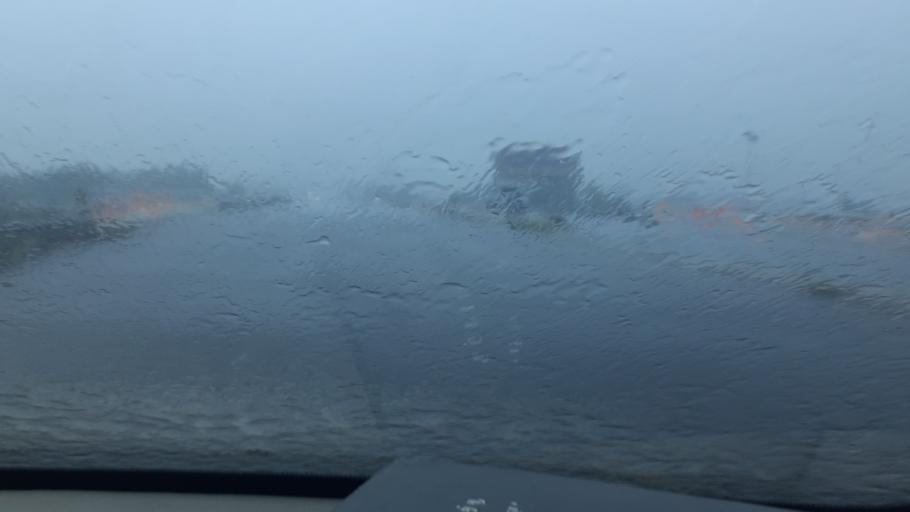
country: IN
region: Tamil Nadu
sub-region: Virudhunagar
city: Sattur
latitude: 9.4522
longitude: 77.9293
